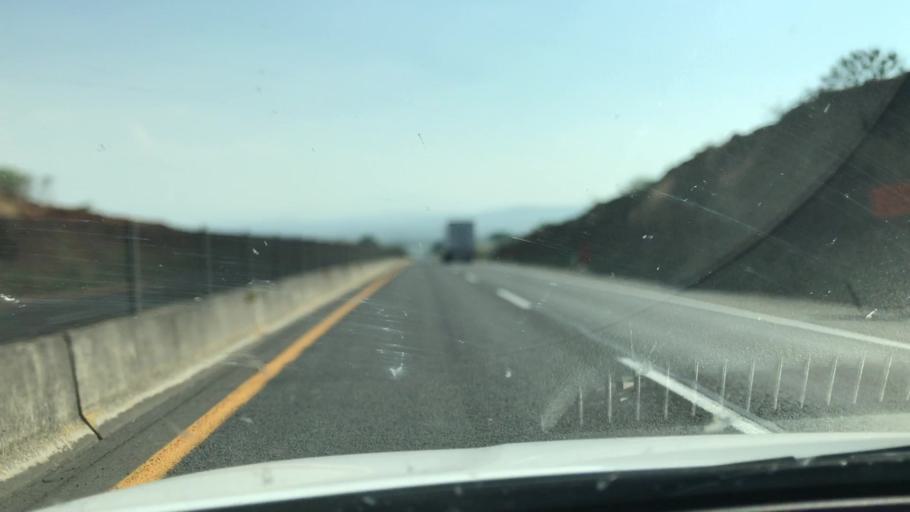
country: MX
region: Jalisco
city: Zapotlanejo
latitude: 20.6443
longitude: -103.0759
